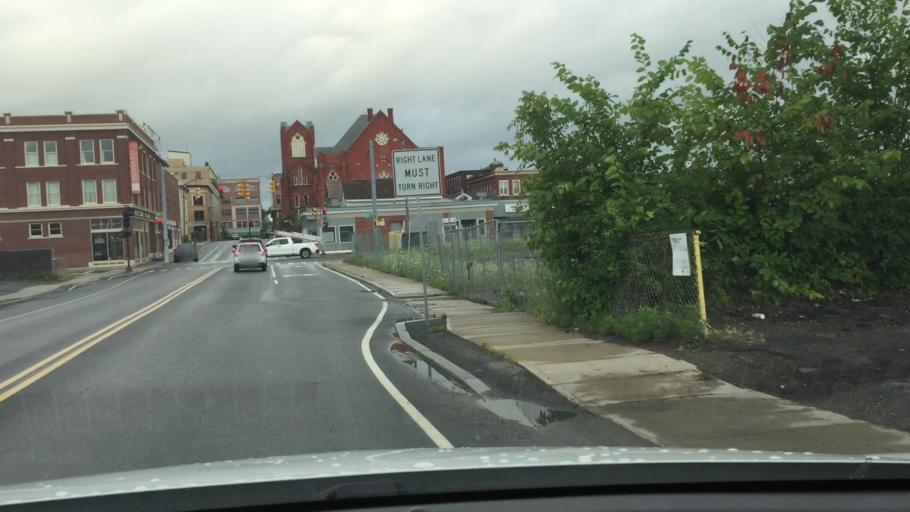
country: US
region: Massachusetts
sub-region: Berkshire County
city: Pittsfield
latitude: 42.4497
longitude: -73.2498
